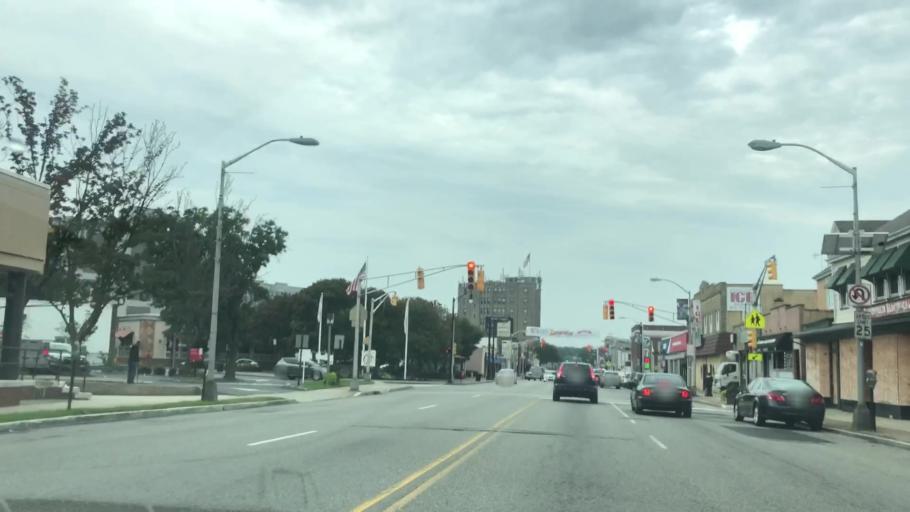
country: US
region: New Jersey
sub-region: Essex County
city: Glen Ridge
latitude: 40.7962
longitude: -74.1998
